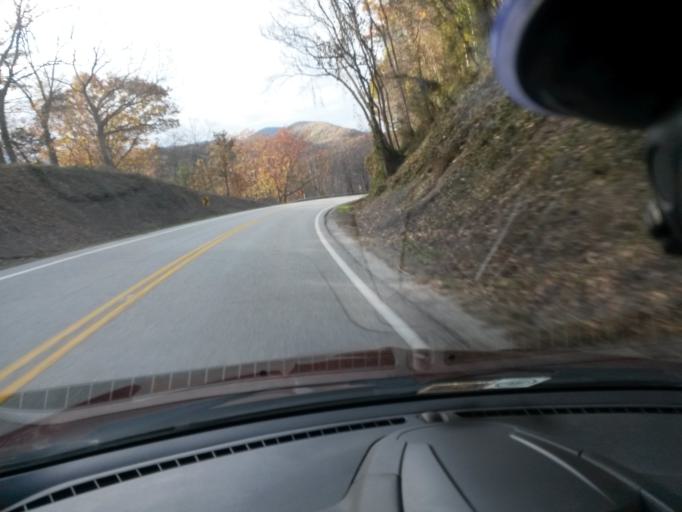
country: US
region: Virginia
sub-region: Rockbridge County
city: Glasgow
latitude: 37.5755
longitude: -79.3717
